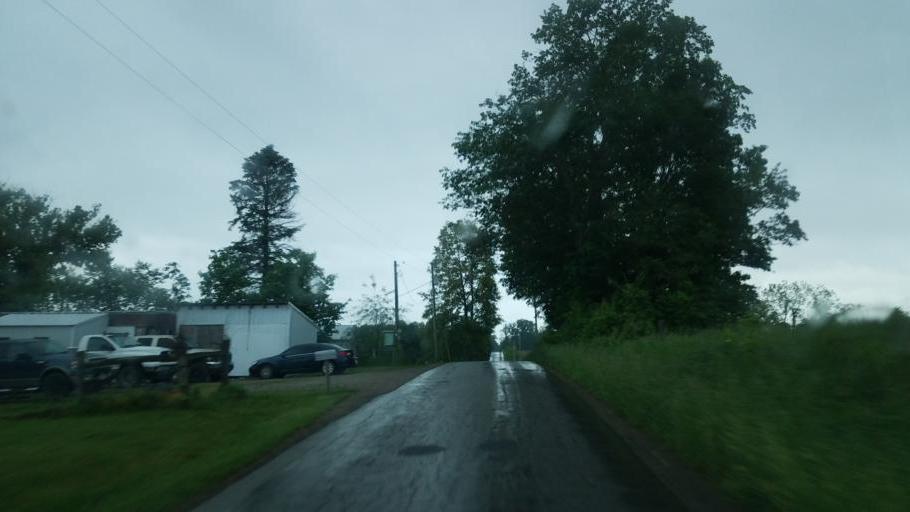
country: US
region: Ohio
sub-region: Knox County
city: Oak Hill
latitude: 40.3239
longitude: -82.2591
